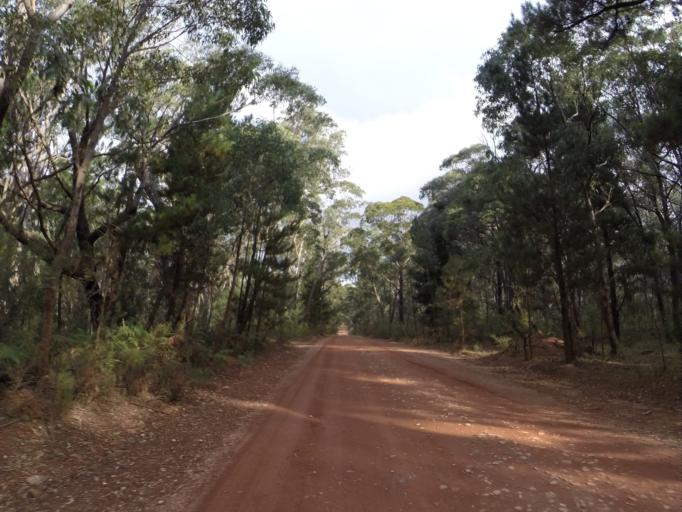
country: AU
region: New South Wales
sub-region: Wingecarribee
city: Bundanoon
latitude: -34.5249
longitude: 150.2128
